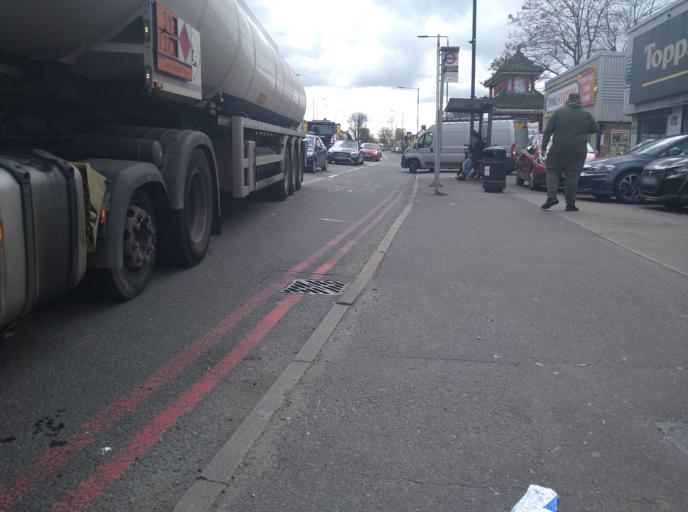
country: GB
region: England
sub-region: Greater London
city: South Croydon
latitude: 51.3636
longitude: -0.1183
